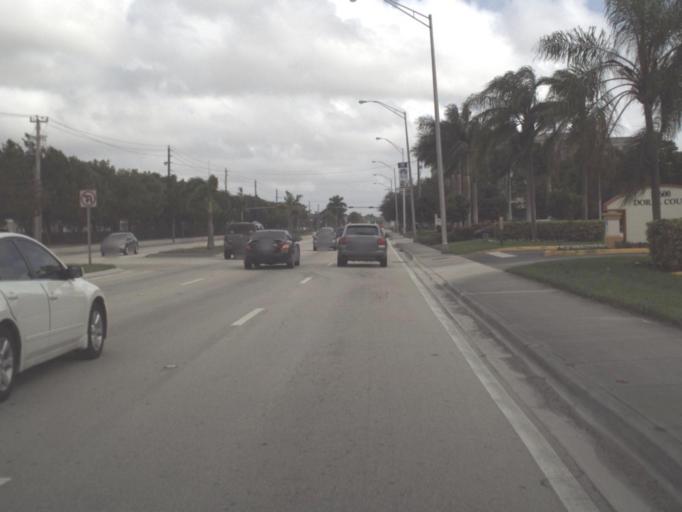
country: US
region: Florida
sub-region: Miami-Dade County
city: Doral
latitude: 25.8097
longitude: -80.3362
